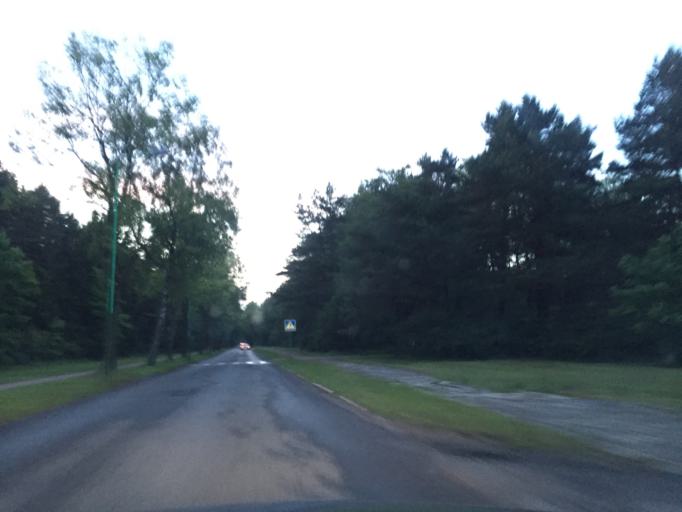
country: LT
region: Klaipedos apskritis
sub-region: Klaipeda
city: Palanga
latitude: 55.8951
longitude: 21.0615
